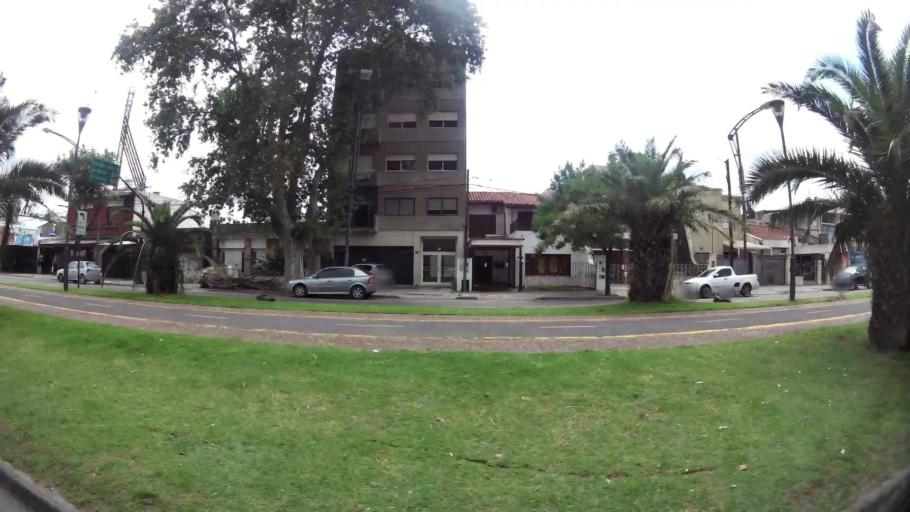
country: AR
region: Santa Fe
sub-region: Departamento de Rosario
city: Rosario
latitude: -32.9757
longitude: -60.6613
